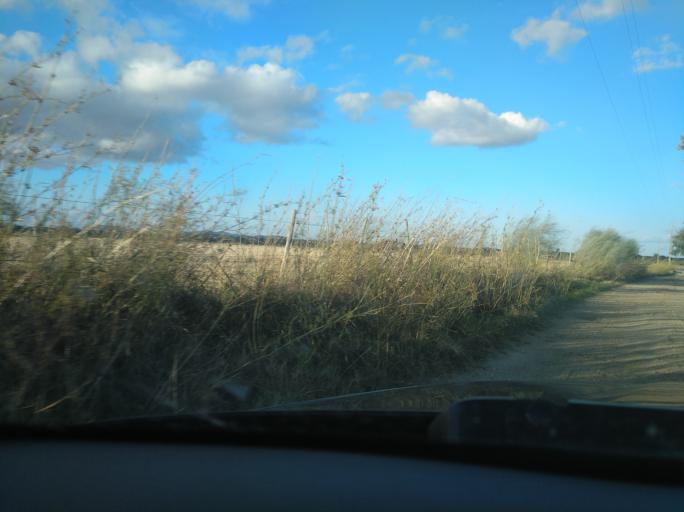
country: PT
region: Portalegre
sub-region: Campo Maior
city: Campo Maior
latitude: 39.0374
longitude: -6.9826
